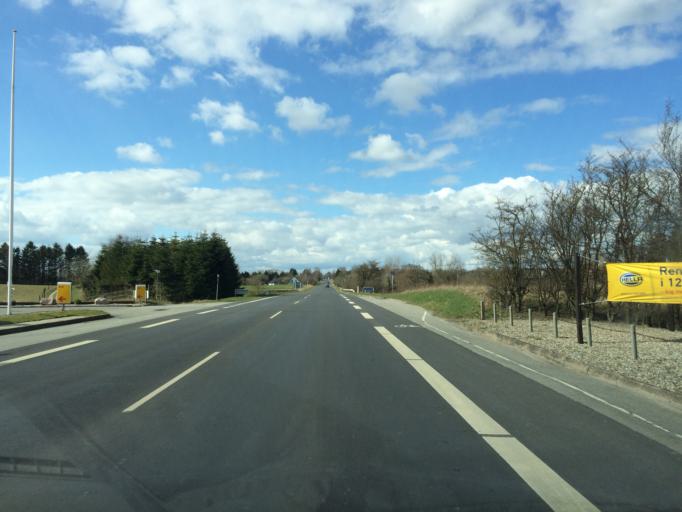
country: DK
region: South Denmark
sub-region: Assens Kommune
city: Arup
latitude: 55.4224
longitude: 10.0329
